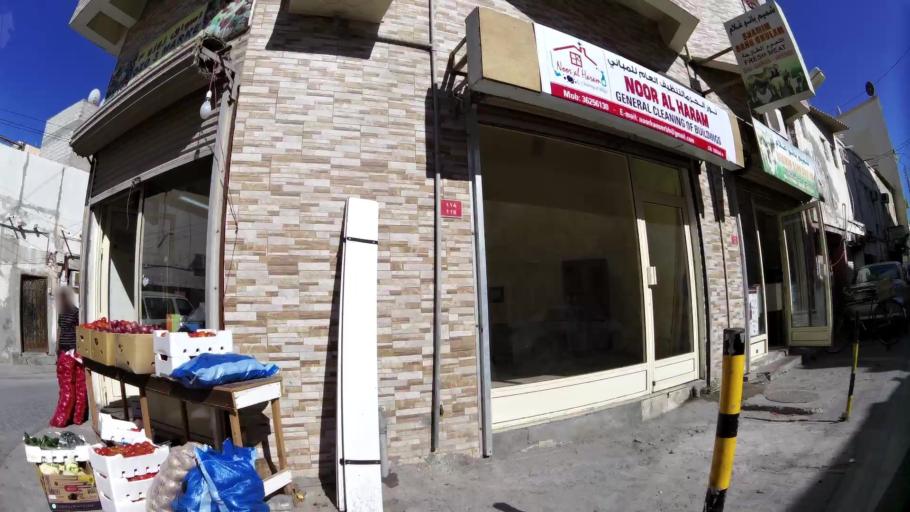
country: BH
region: Muharraq
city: Al Muharraq
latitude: 26.2562
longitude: 50.6115
